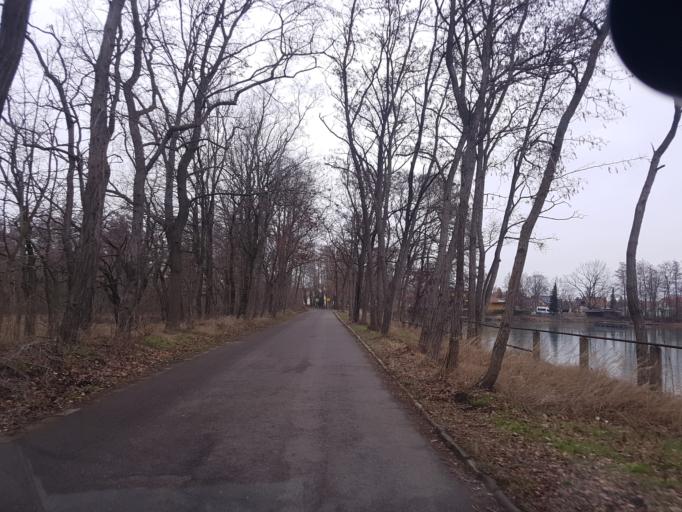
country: DE
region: Brandenburg
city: Falkenberg
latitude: 51.5831
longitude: 13.2609
